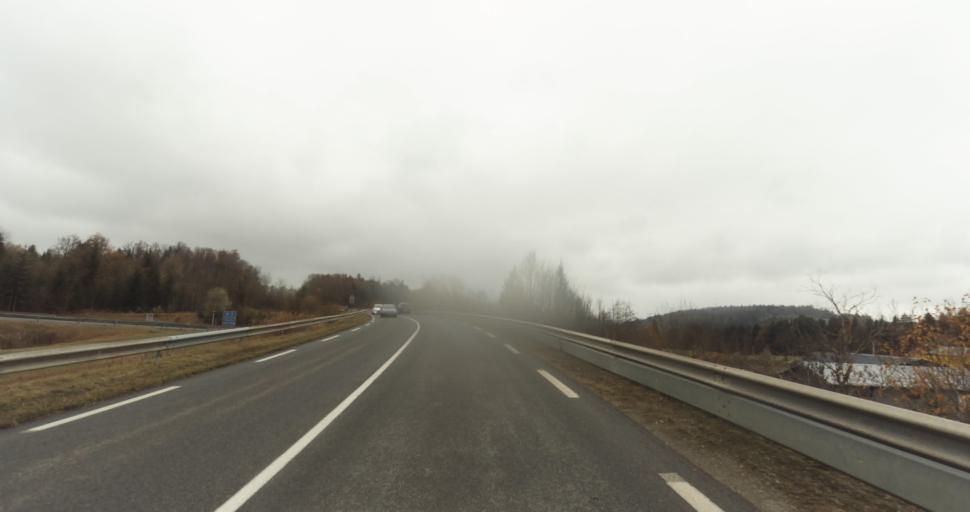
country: FR
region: Rhone-Alpes
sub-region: Departement de la Haute-Savoie
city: Evires
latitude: 46.0412
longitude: 6.2476
